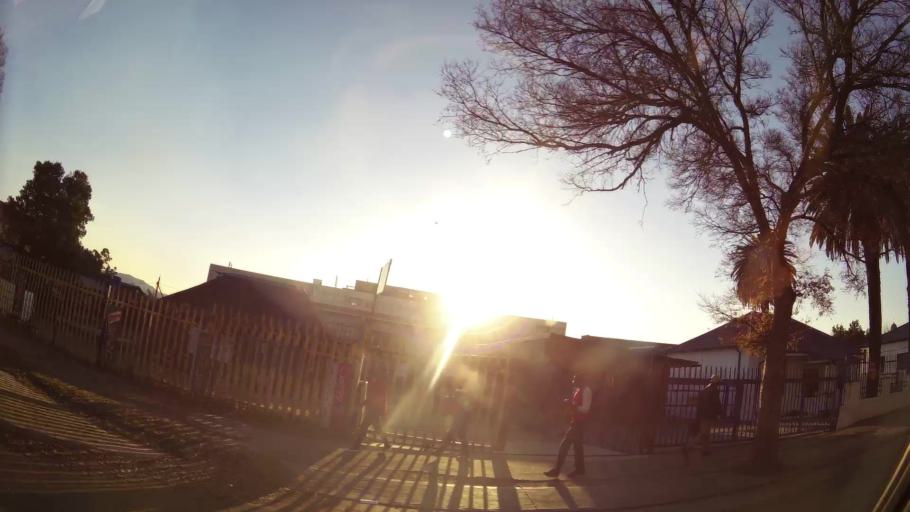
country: ZA
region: Gauteng
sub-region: Ekurhuleni Metropolitan Municipality
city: Germiston
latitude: -26.2589
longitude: 28.1292
